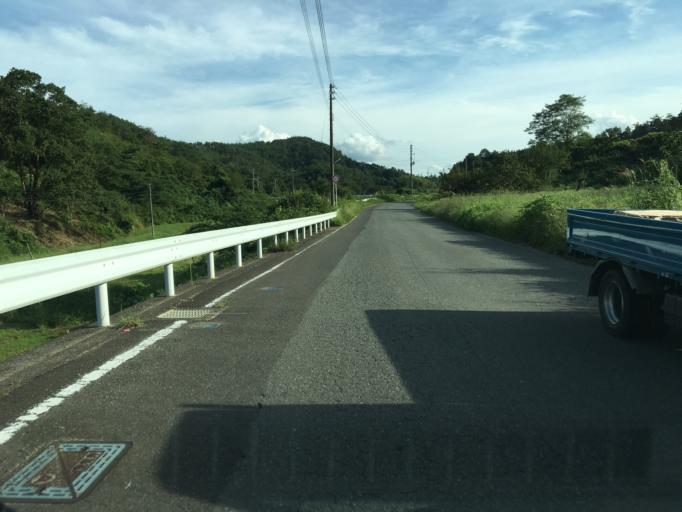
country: JP
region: Fukushima
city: Hobaramachi
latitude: 37.8072
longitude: 140.5893
